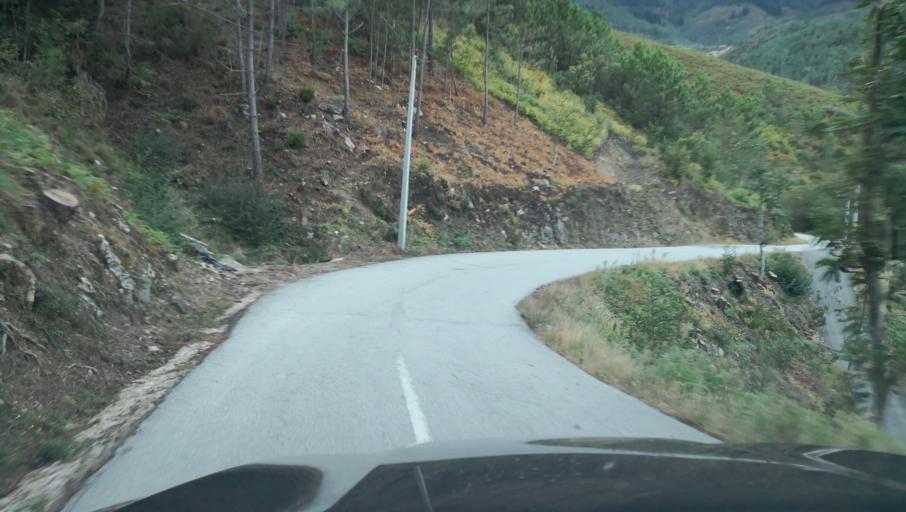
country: PT
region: Vila Real
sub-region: Santa Marta de Penaguiao
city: Santa Marta de Penaguiao
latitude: 41.2610
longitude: -7.8630
